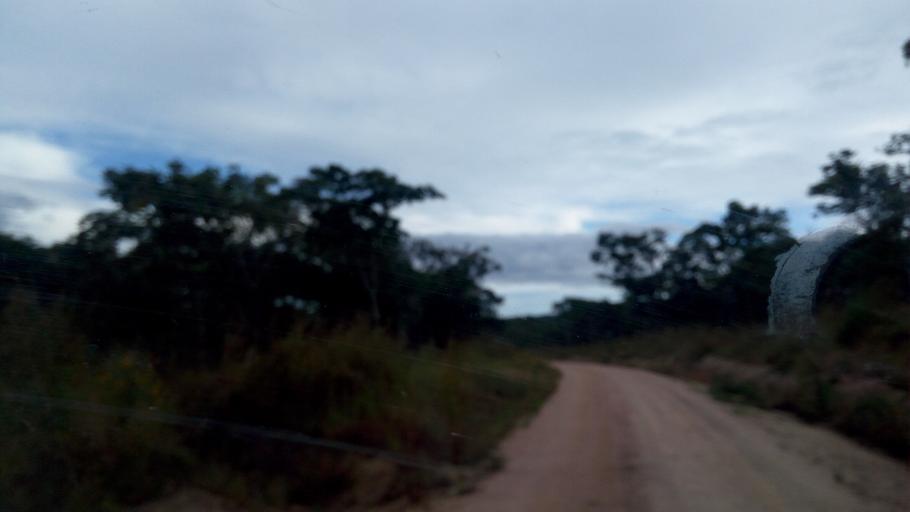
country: CD
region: Katanga
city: Kalemie
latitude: -6.5979
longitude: 29.0415
